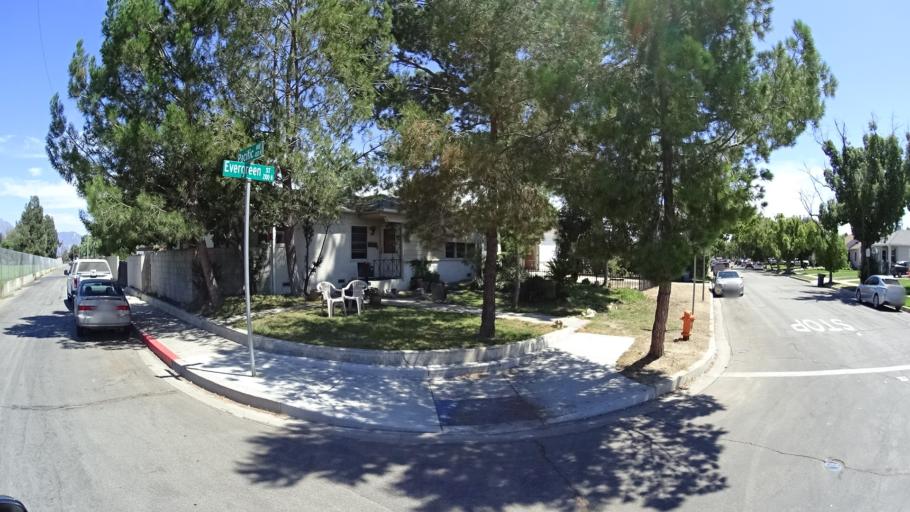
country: US
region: California
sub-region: Los Angeles County
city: North Hollywood
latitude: 34.1885
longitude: -118.3554
